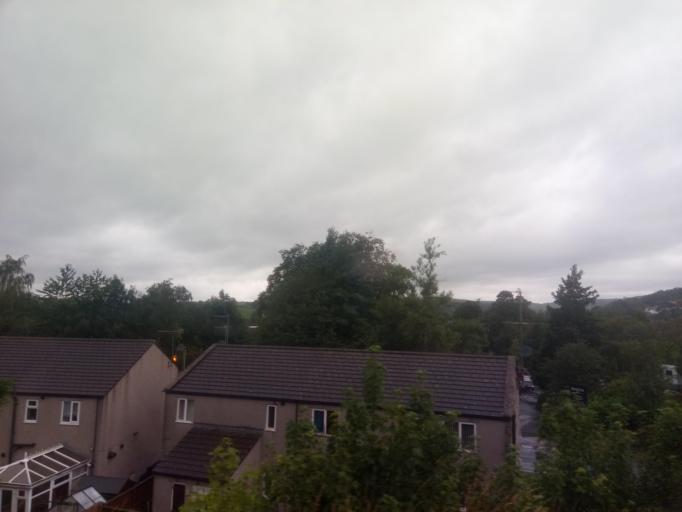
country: GB
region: England
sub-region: North Yorkshire
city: Settle
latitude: 54.0679
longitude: -2.2802
